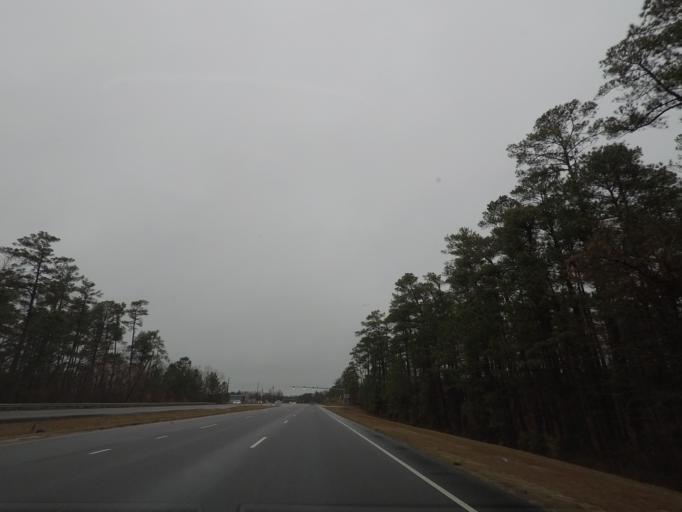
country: US
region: North Carolina
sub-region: Cumberland County
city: Spring Lake
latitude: 35.2419
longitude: -79.0217
